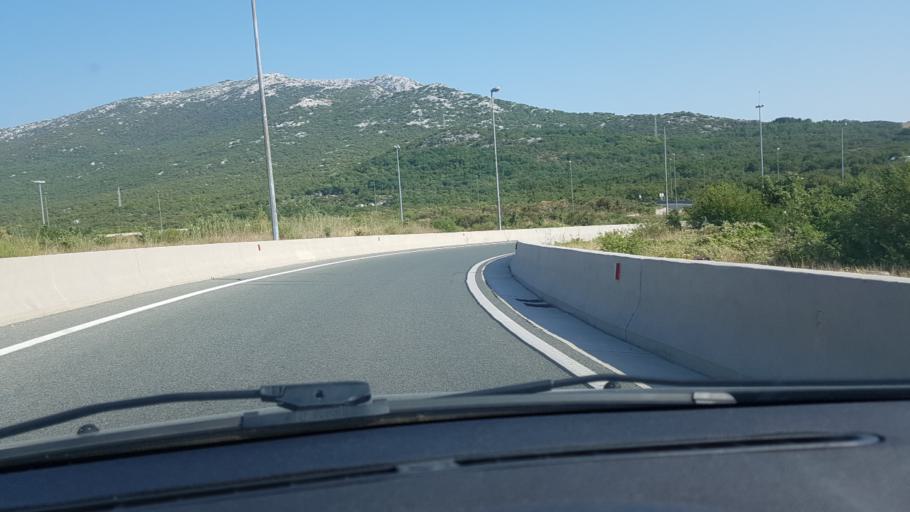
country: HR
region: Splitsko-Dalmatinska
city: Klis
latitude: 43.5760
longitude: 16.5378
